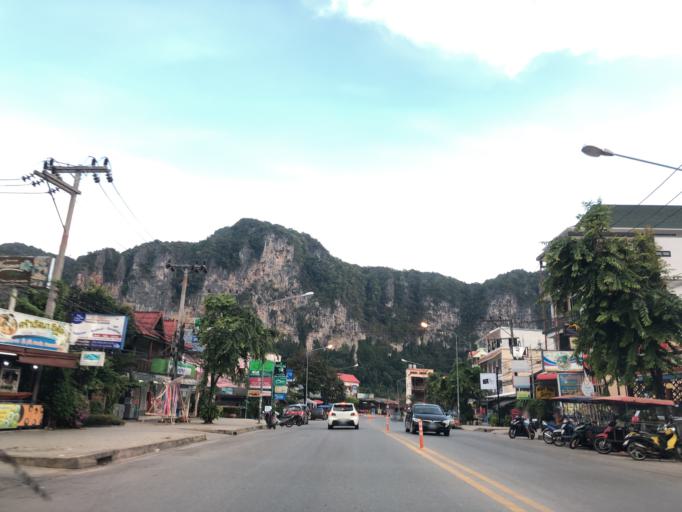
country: TH
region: Phangnga
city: Ban Ao Nang
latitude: 8.0372
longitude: 98.8336
